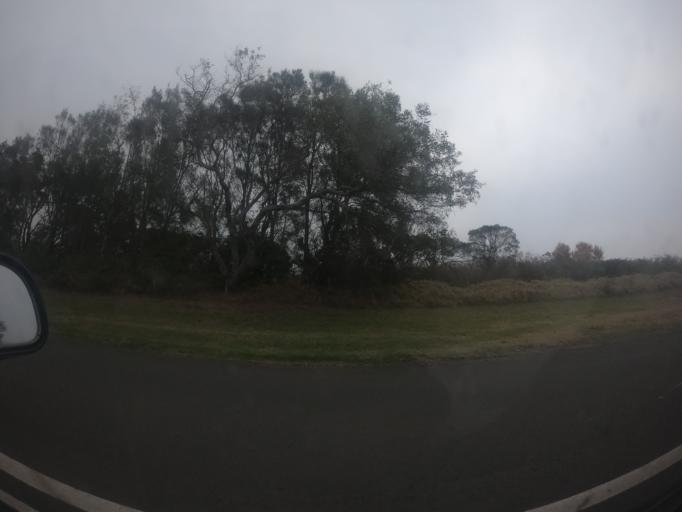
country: AU
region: New South Wales
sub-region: Shellharbour
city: Shellharbour Village
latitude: -34.6065
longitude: 150.8617
